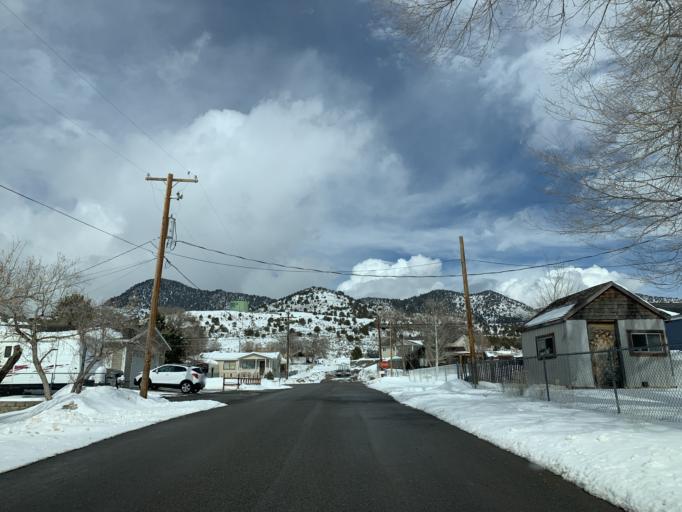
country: US
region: Utah
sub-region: Utah County
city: Genola
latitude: 39.9569
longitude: -112.1117
